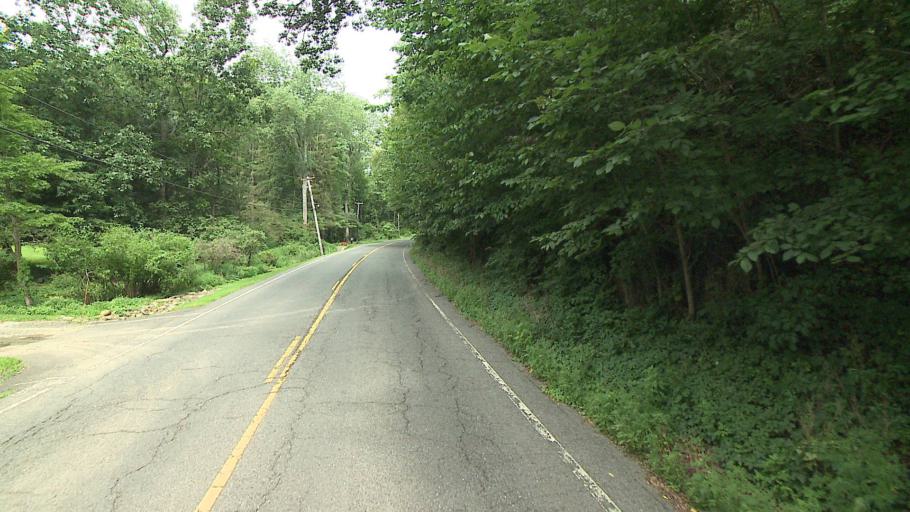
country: US
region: Connecticut
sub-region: Fairfield County
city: Sherman
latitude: 41.6418
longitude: -73.5014
